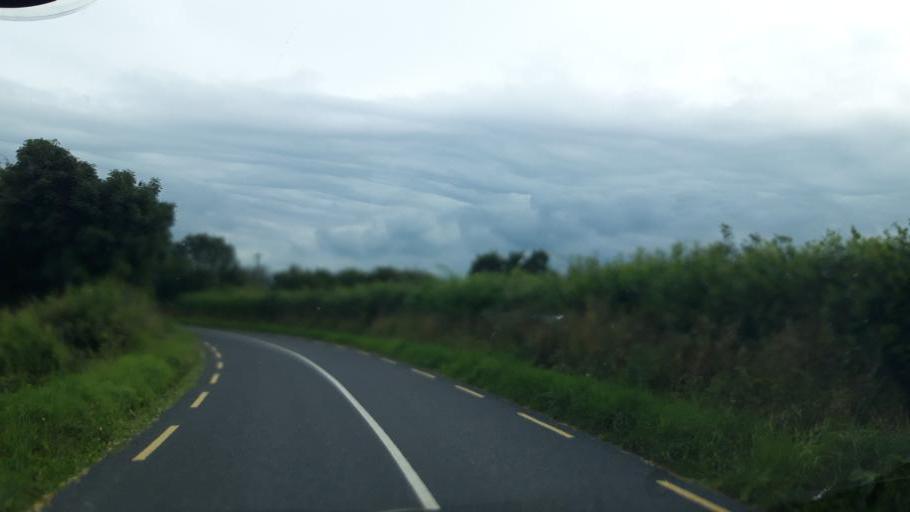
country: IE
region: Leinster
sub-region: Kilkenny
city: Ballyragget
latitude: 52.7523
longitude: -7.3920
